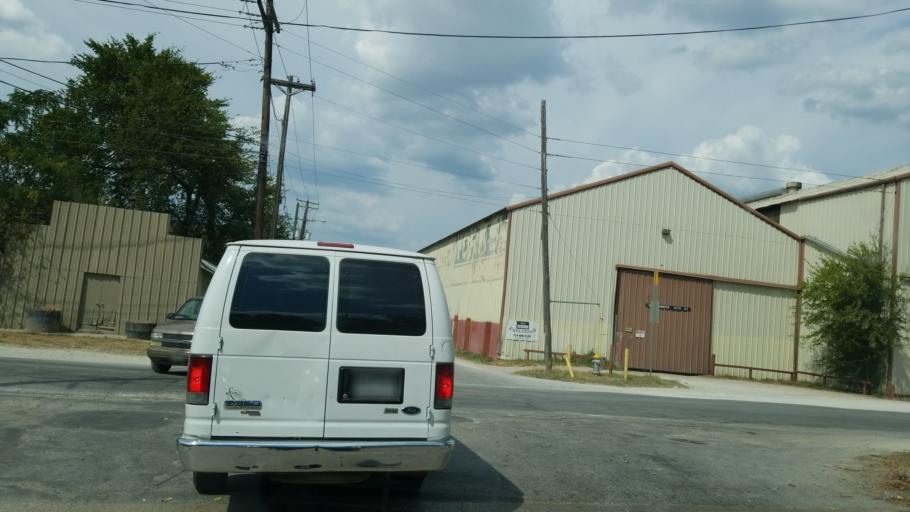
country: US
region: Texas
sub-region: Dallas County
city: Dallas
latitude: 32.7725
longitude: -96.8480
